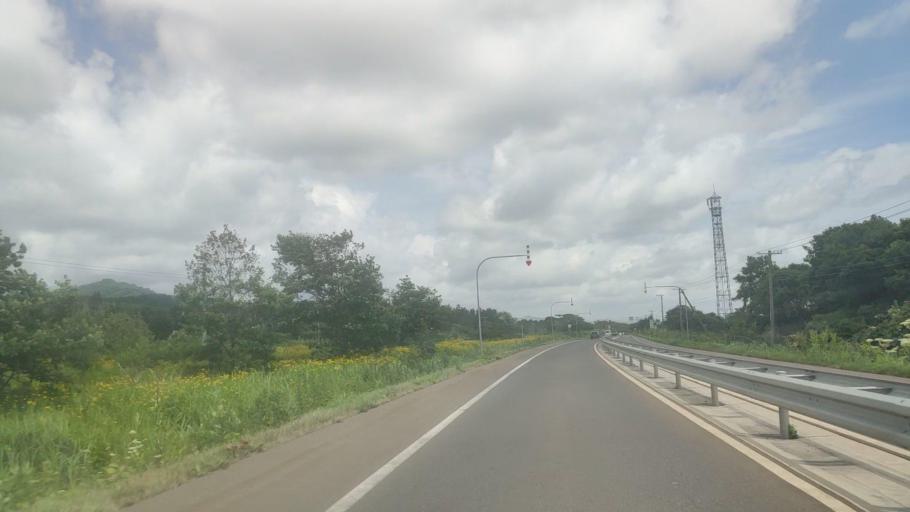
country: JP
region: Hokkaido
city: Niseko Town
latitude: 42.4547
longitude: 140.3326
